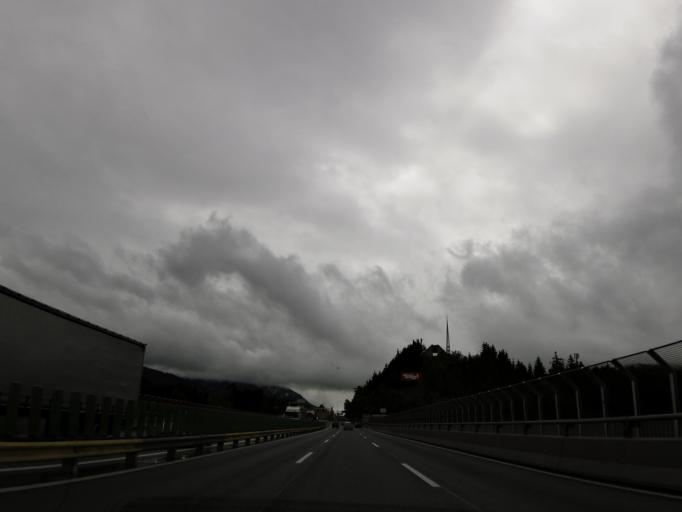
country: AT
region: Tyrol
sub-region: Politischer Bezirk Innsbruck Land
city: Patsch
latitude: 47.2013
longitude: 11.3999
